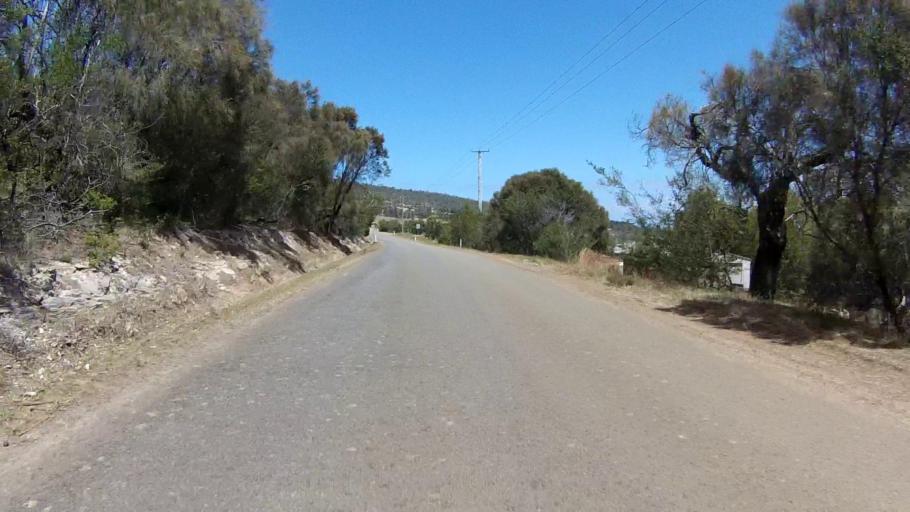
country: AU
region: Tasmania
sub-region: Clarence
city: Lauderdale
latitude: -42.9277
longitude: 147.4658
